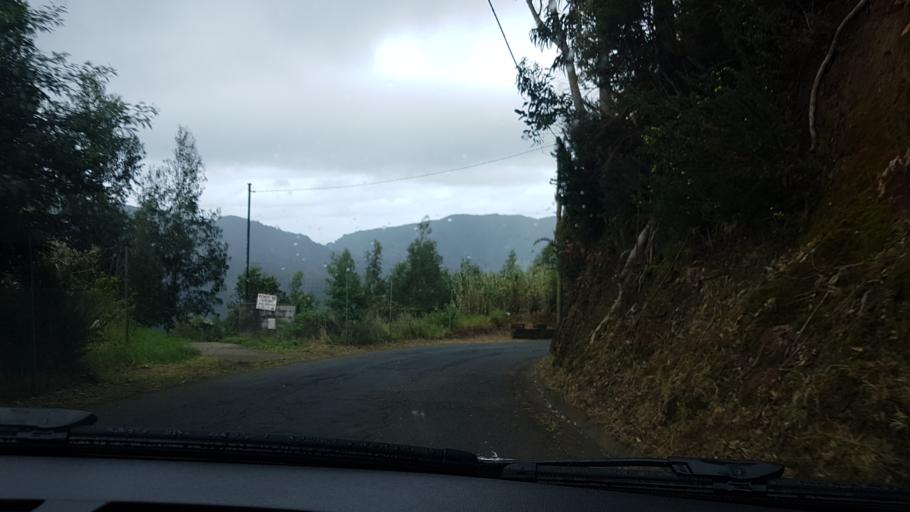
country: PT
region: Madeira
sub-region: Santa Cruz
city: Santa Cruz
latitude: 32.7286
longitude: -16.8110
